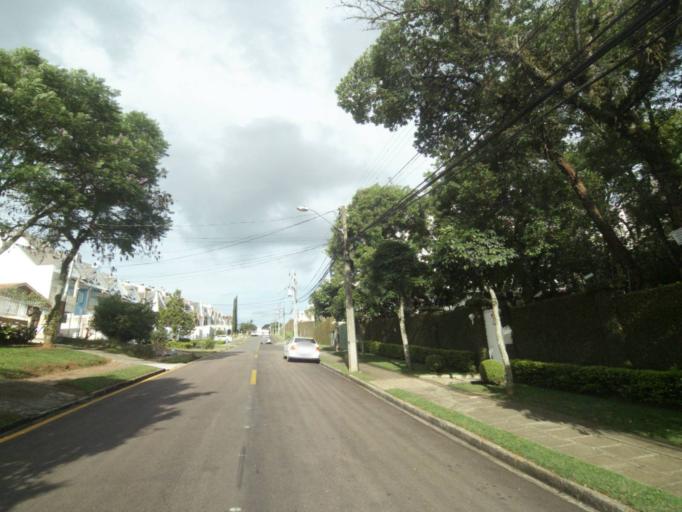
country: BR
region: Parana
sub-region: Curitiba
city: Curitiba
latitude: -25.4424
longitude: -49.3111
